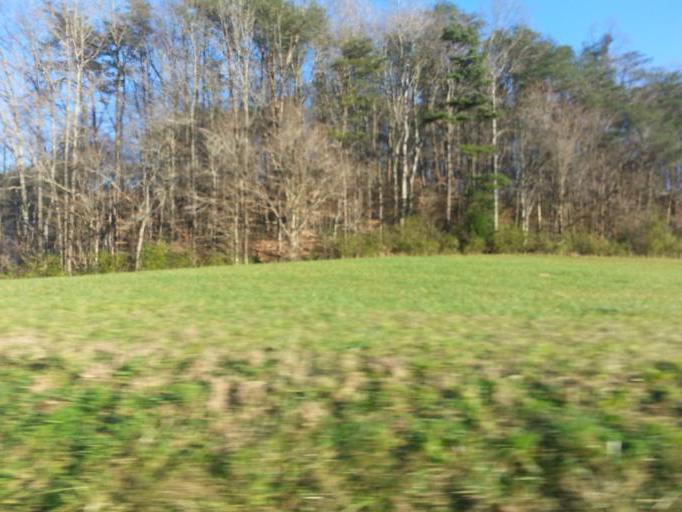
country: US
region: Tennessee
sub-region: Anderson County
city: Clinton
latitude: 36.1163
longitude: -84.2068
